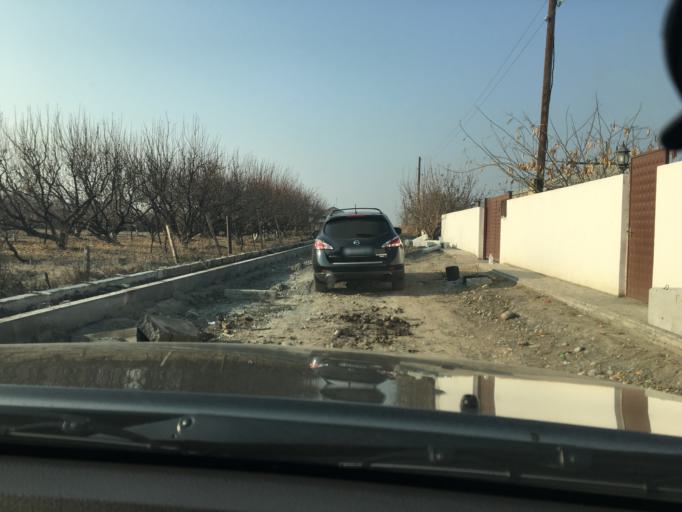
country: AM
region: Armavir
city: Janfida
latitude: 40.0393
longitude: 44.0130
